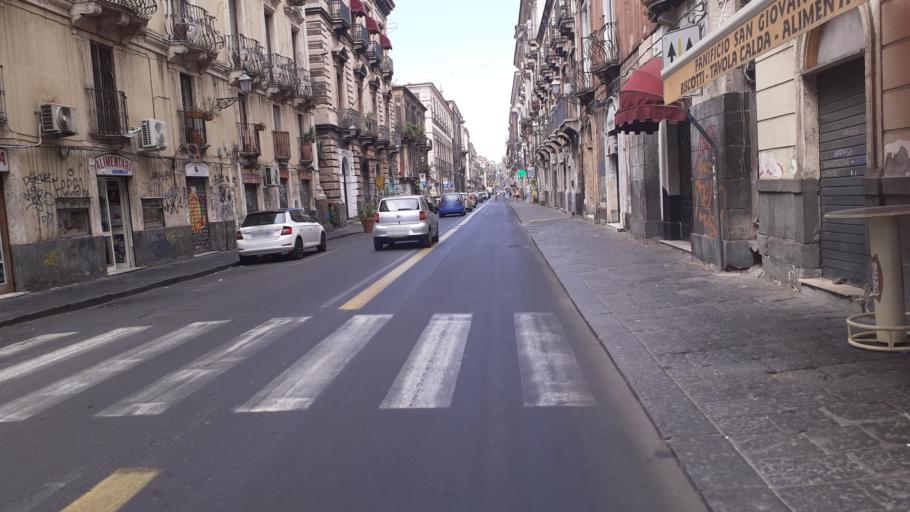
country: IT
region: Sicily
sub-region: Catania
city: Catania
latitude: 37.5033
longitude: 15.0920
